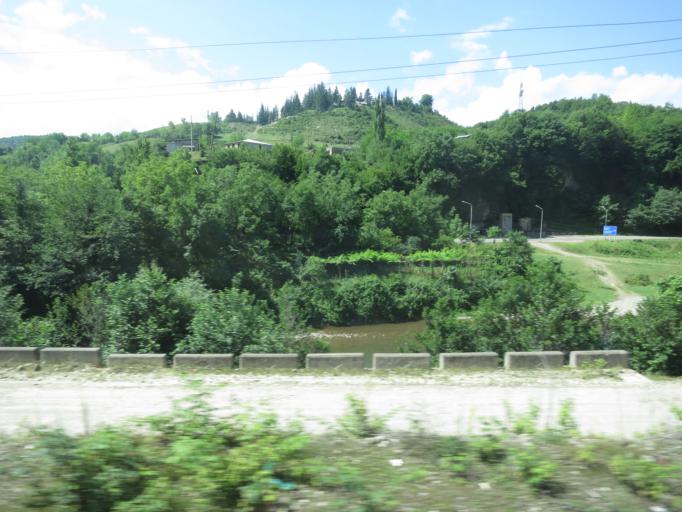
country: GE
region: Imereti
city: Kharagauli
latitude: 42.0283
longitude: 43.1957
